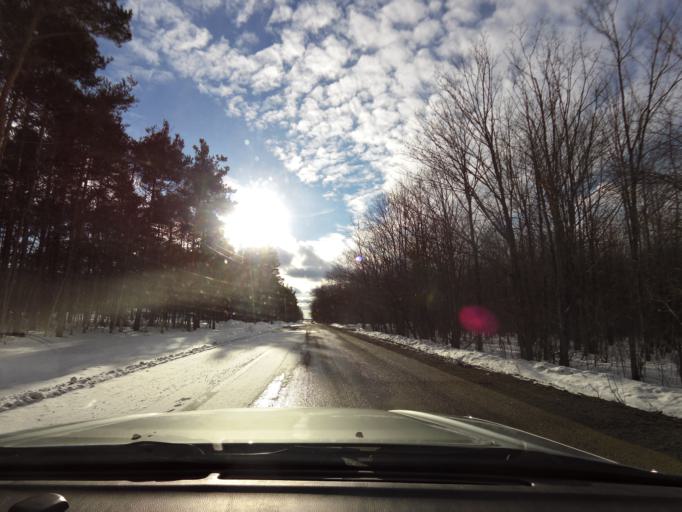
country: US
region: New York
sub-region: Cattaraugus County
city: Franklinville
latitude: 42.3377
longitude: -78.4178
